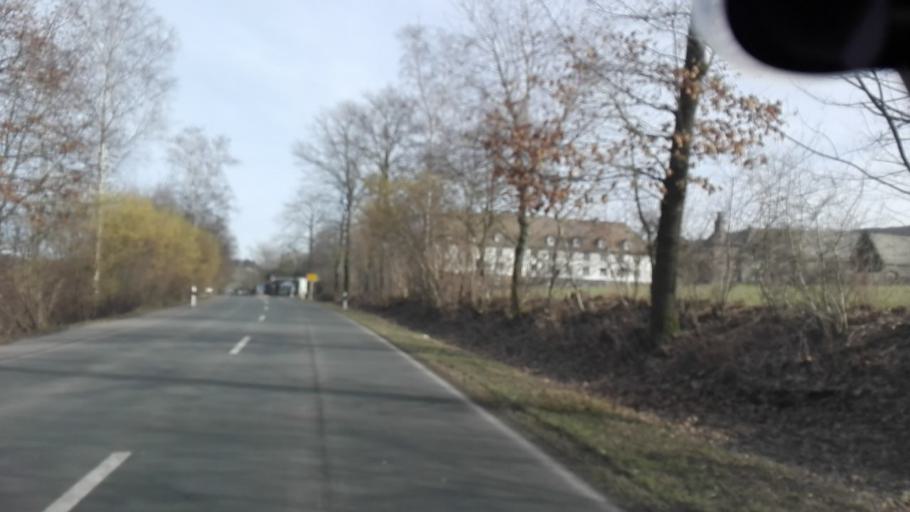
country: DE
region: North Rhine-Westphalia
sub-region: Regierungsbezirk Arnsberg
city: Schmallenberg
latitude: 51.1453
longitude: 8.3200
